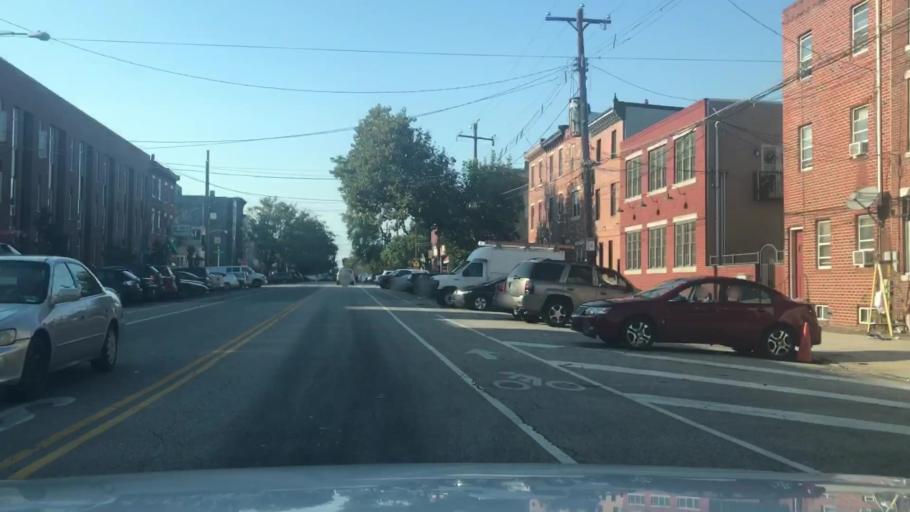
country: US
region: Pennsylvania
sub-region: Philadelphia County
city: Philadelphia
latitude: 39.9782
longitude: -75.1248
